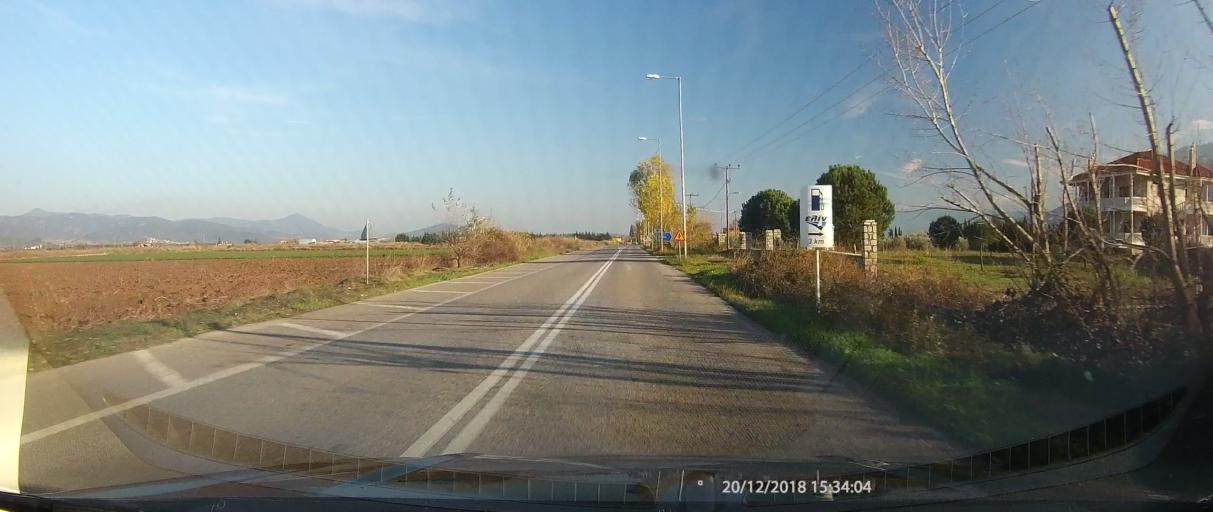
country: GR
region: Central Greece
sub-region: Nomos Fthiotidos
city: Lianokladhion
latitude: 38.9205
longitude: 22.2885
